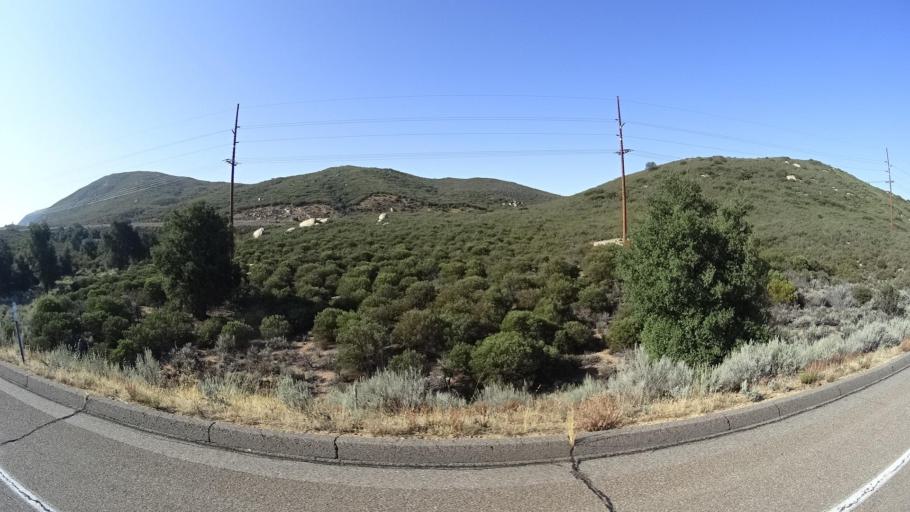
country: US
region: California
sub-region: San Diego County
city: Pine Valley
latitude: 32.8165
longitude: -116.5170
